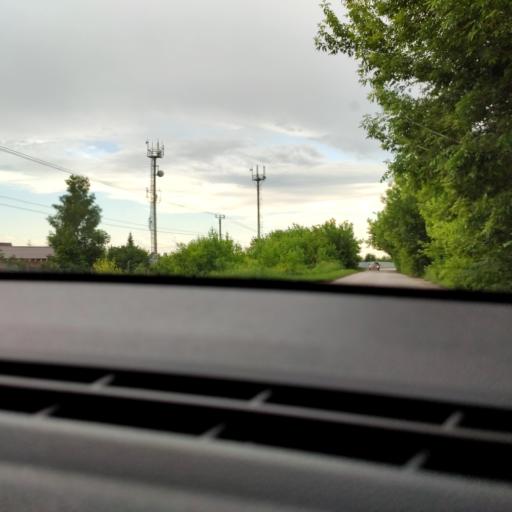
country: RU
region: Samara
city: Podstepki
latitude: 53.5148
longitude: 49.0714
